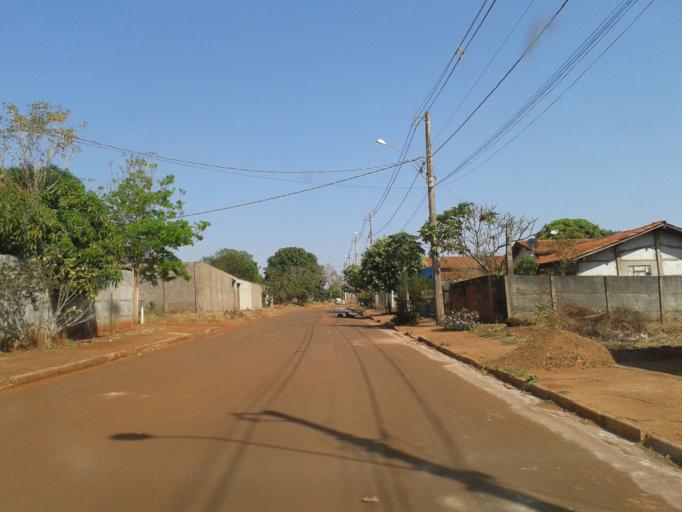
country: BR
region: Minas Gerais
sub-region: Ituiutaba
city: Ituiutaba
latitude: -18.9574
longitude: -49.4783
